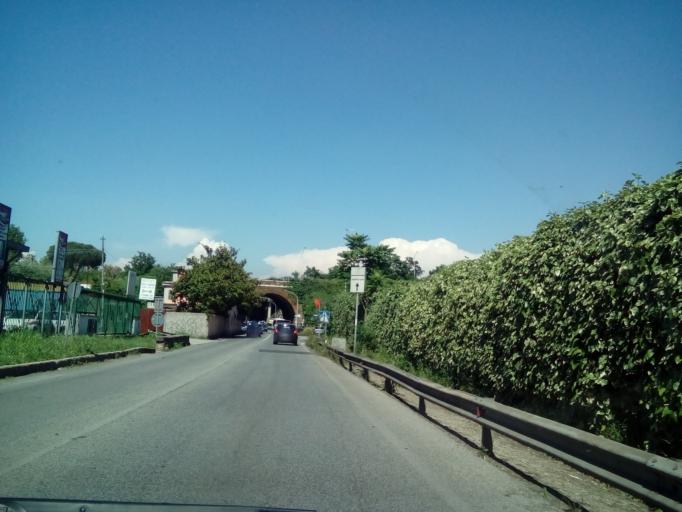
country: VA
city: Vatican City
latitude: 41.8415
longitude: 12.4660
